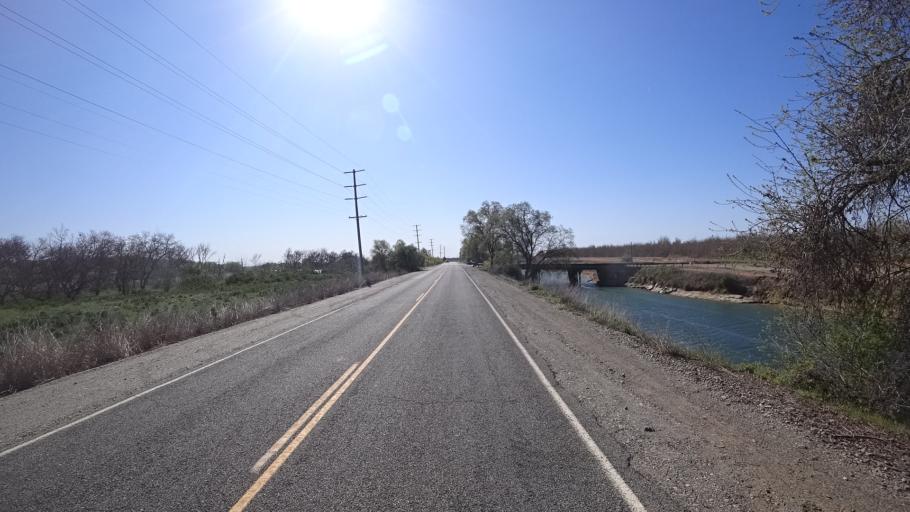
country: US
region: California
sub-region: Glenn County
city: Hamilton City
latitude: 39.7672
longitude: -122.0316
